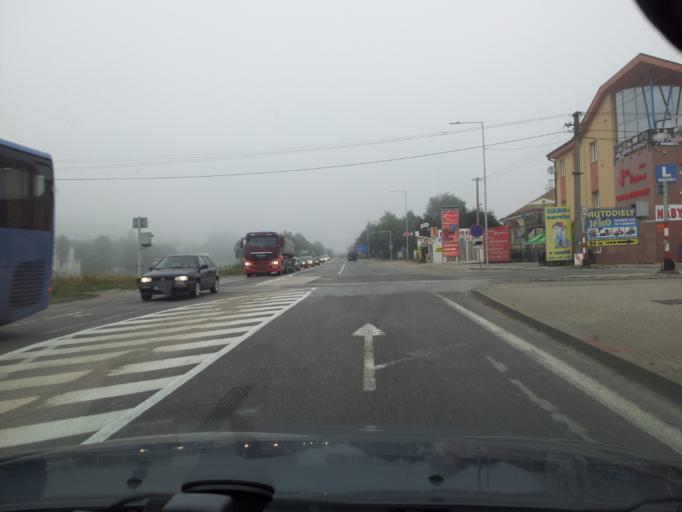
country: SK
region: Zilinsky
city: Cadca
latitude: 49.4430
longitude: 18.7863
